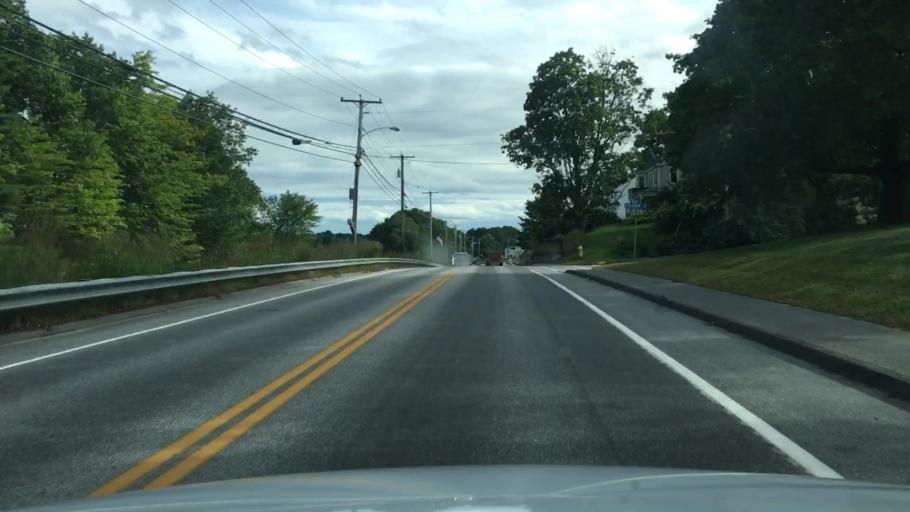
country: US
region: Maine
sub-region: Kennebec County
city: Farmingdale
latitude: 44.2502
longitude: -69.7720
